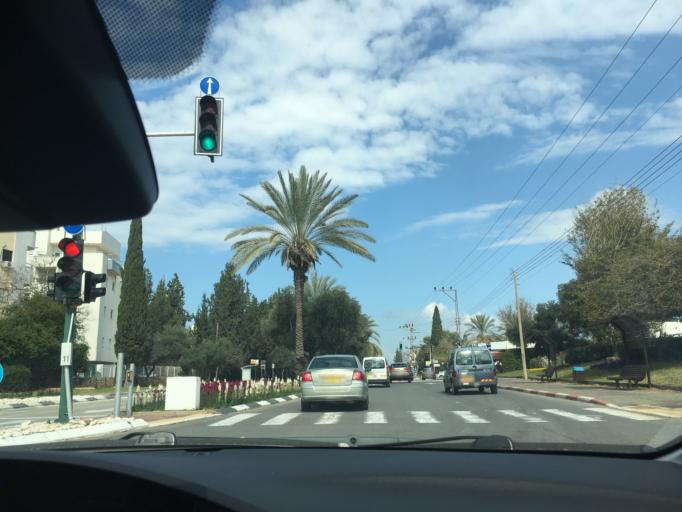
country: IL
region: Tel Aviv
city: Ramat HaSharon
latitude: 32.1678
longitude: 34.8529
